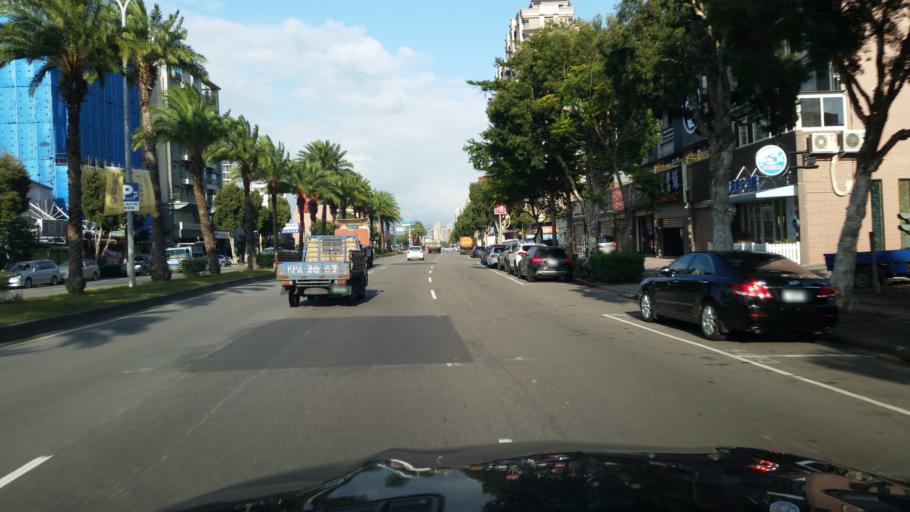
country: TW
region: Taiwan
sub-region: Taoyuan
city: Taoyuan
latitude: 25.0707
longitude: 121.3578
